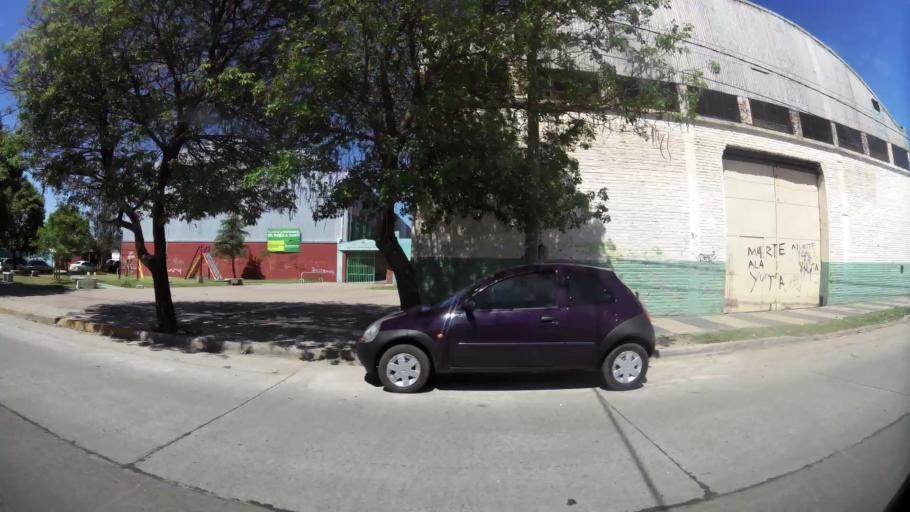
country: AR
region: Cordoba
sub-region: Departamento de Capital
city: Cordoba
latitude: -31.3760
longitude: -64.1478
